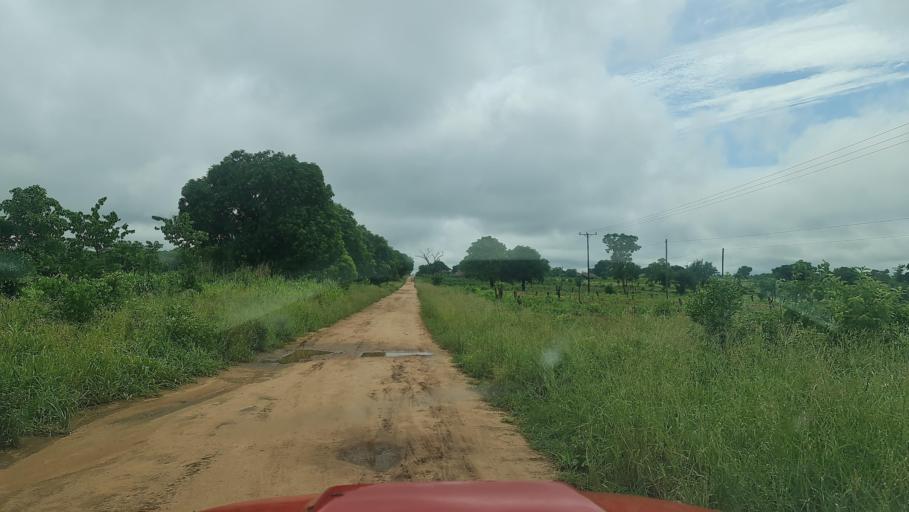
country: MW
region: Southern Region
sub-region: Nsanje District
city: Nsanje
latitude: -17.1855
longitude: 35.9177
